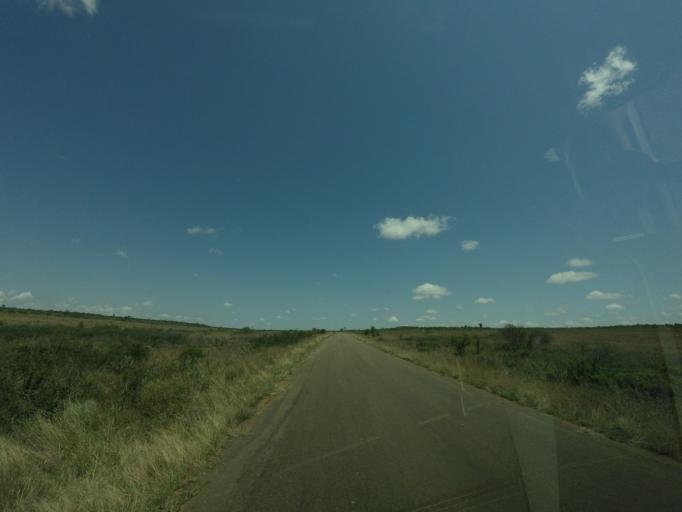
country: ZA
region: Mpumalanga
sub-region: Ehlanzeni District
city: Komatipoort
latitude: -24.8934
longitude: 31.9123
